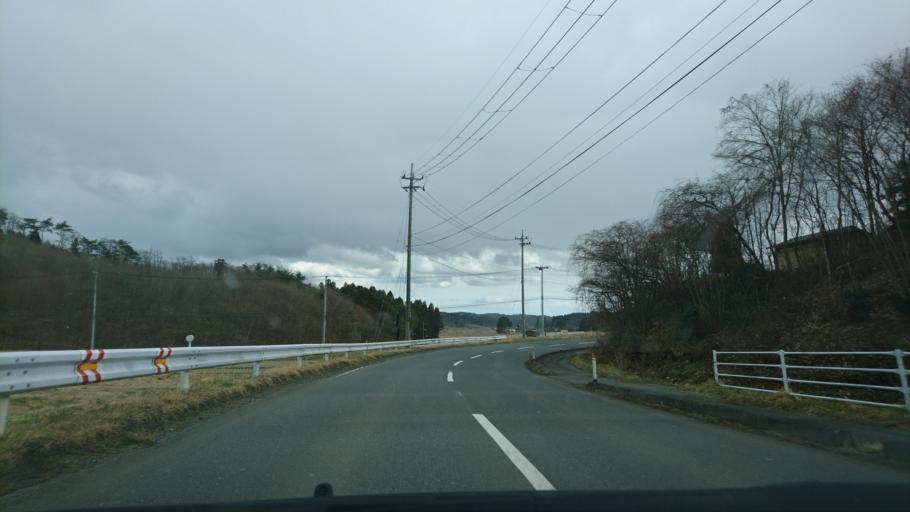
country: JP
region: Iwate
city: Ichinoseki
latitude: 38.8276
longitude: 141.1735
